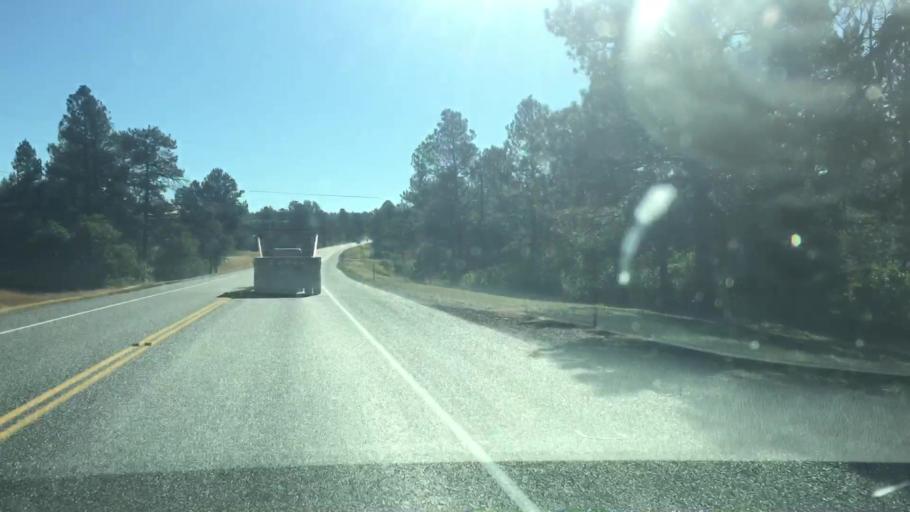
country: US
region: Colorado
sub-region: Douglas County
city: The Pinery
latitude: 39.3885
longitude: -104.7408
